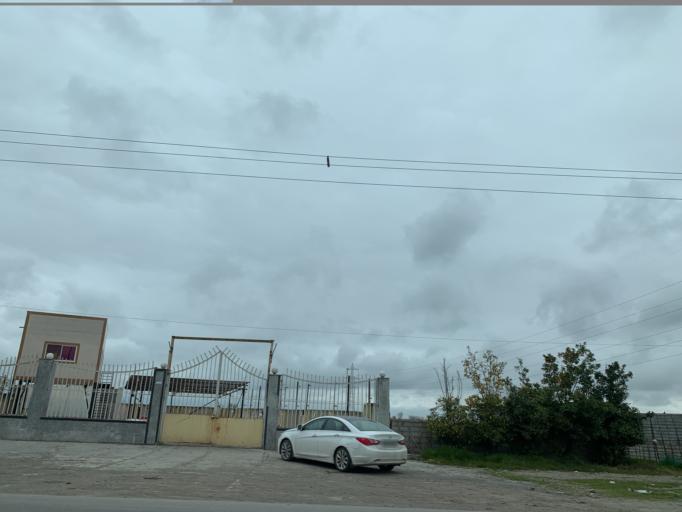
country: IR
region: Mazandaran
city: Babol
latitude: 36.5135
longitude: 52.5625
